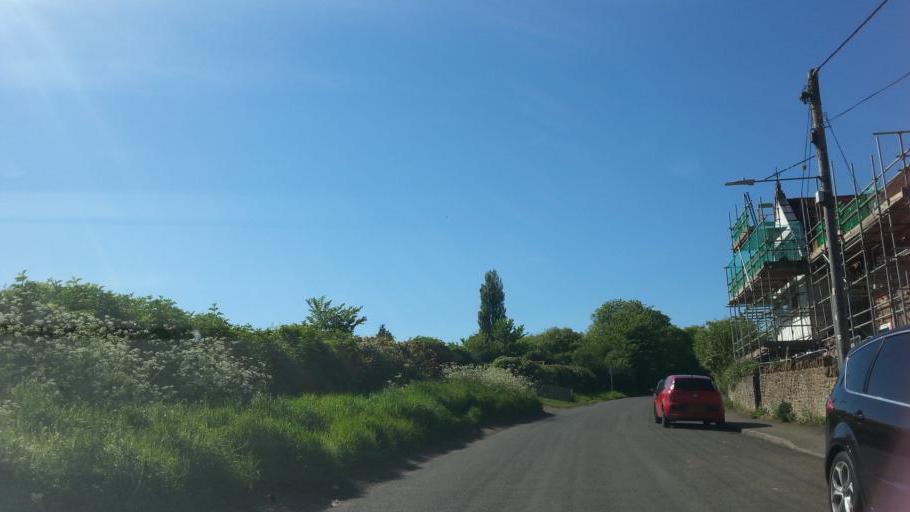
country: GB
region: England
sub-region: Somerset
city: Milborne Port
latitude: 50.9673
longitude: -2.4695
